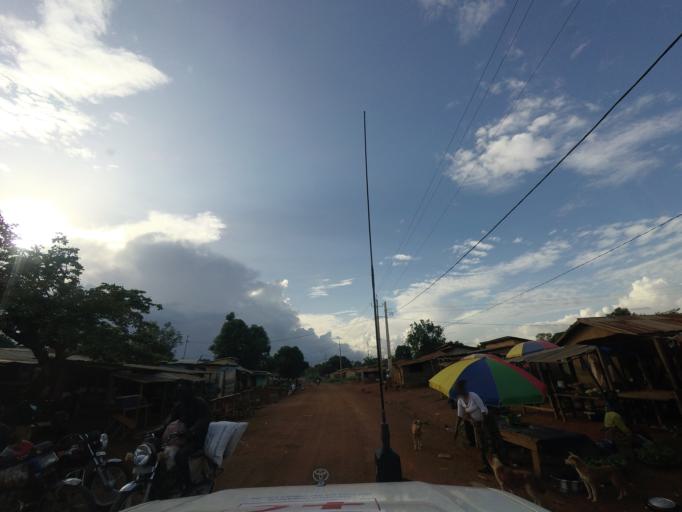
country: GN
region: Nzerekore
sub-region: Nzerekore Prefecture
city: Nzerekore
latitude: 7.7292
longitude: -8.8271
